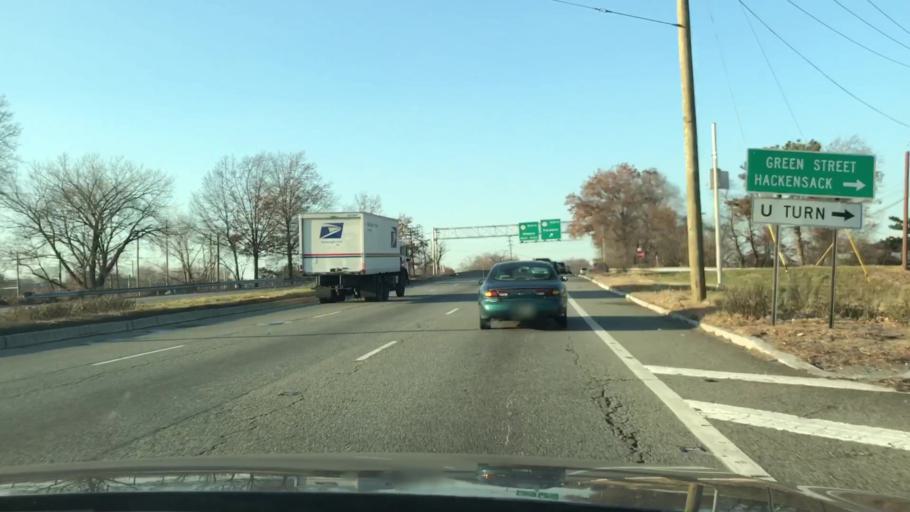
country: US
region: New Jersey
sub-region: Bergen County
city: Hasbrouck Heights
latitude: 40.8636
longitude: -74.0608
